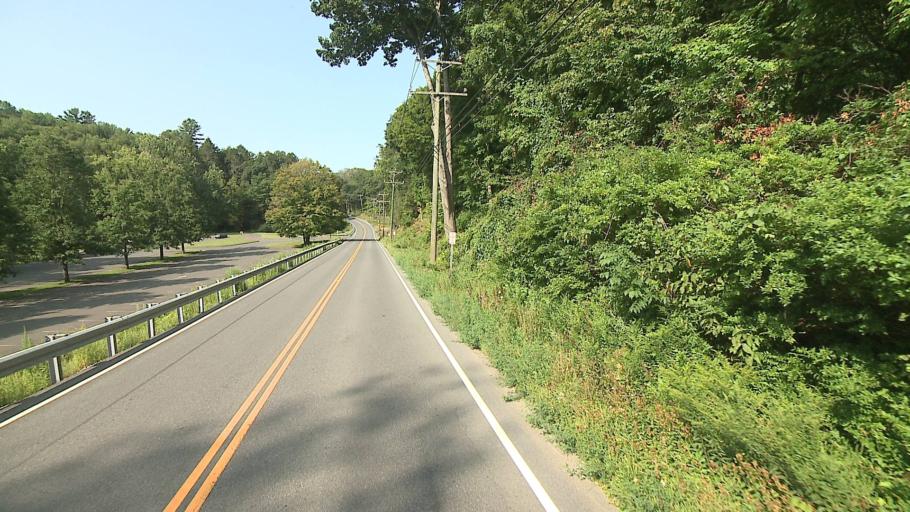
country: US
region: Connecticut
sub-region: Litchfield County
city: Kent
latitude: 41.7772
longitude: -73.4166
